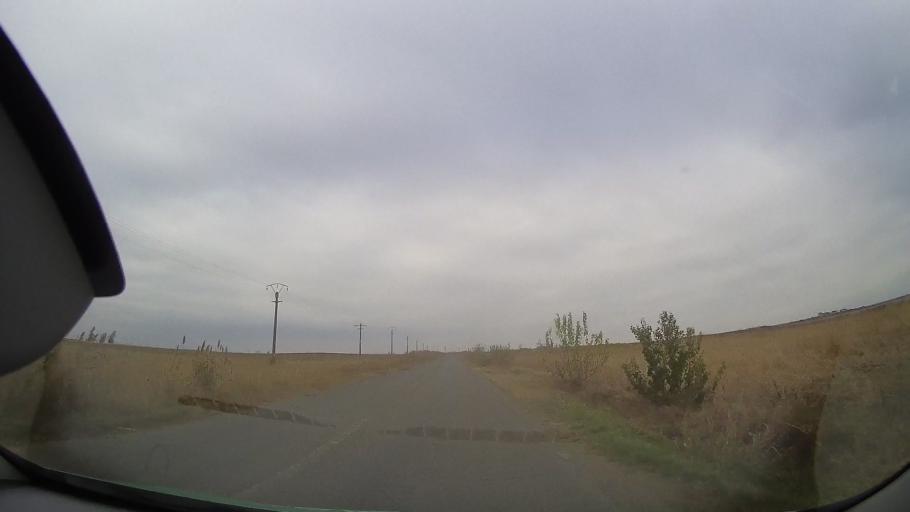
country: RO
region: Buzau
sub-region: Comuna Luciu
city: Luciu
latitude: 44.9667
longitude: 27.1108
